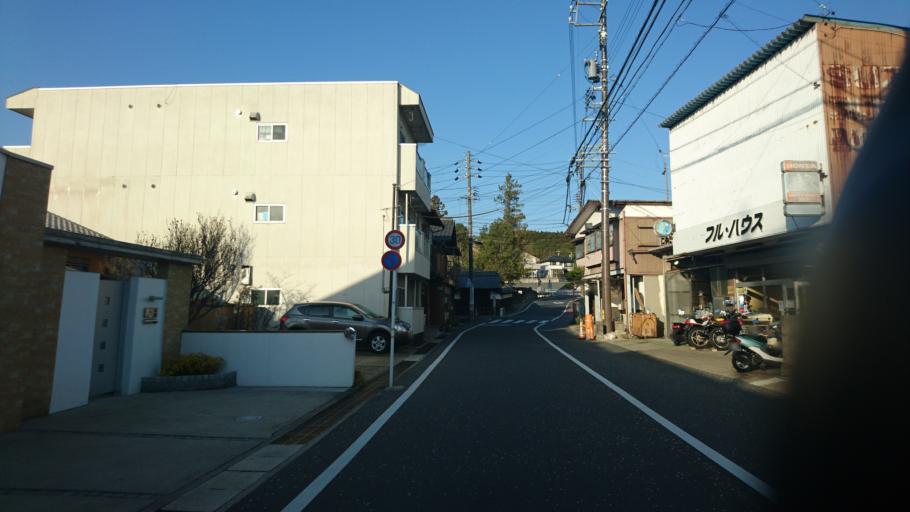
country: JP
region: Gifu
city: Nakatsugawa
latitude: 35.4554
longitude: 137.4145
